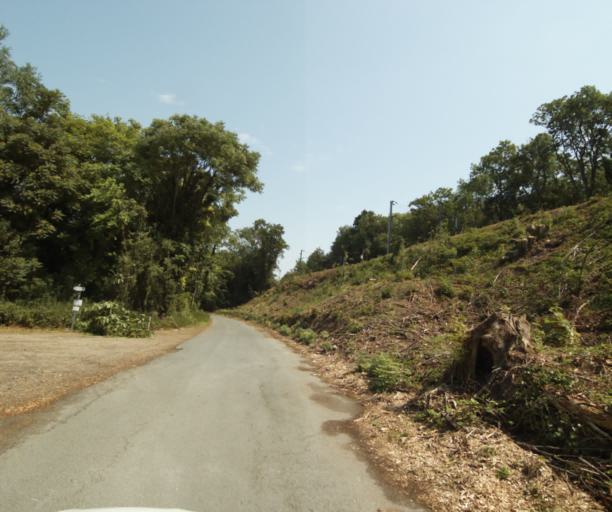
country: FR
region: Ile-de-France
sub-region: Departement des Yvelines
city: Maurecourt
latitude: 49.0023
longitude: 2.0730
